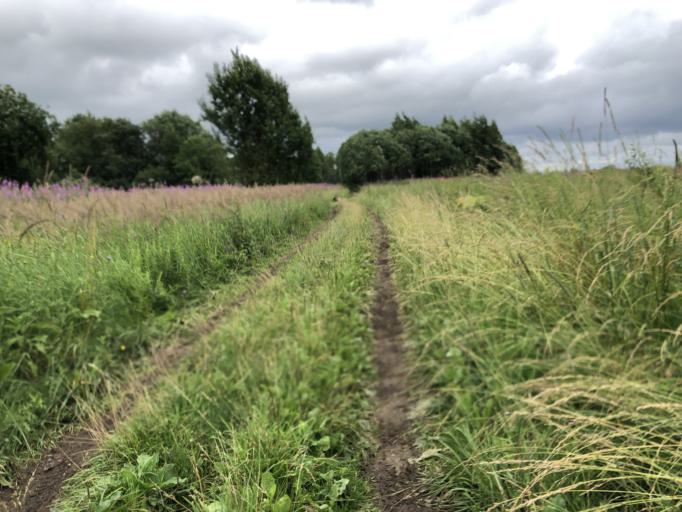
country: RU
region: Tverskaya
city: Rzhev
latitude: 56.2382
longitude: 34.3831
